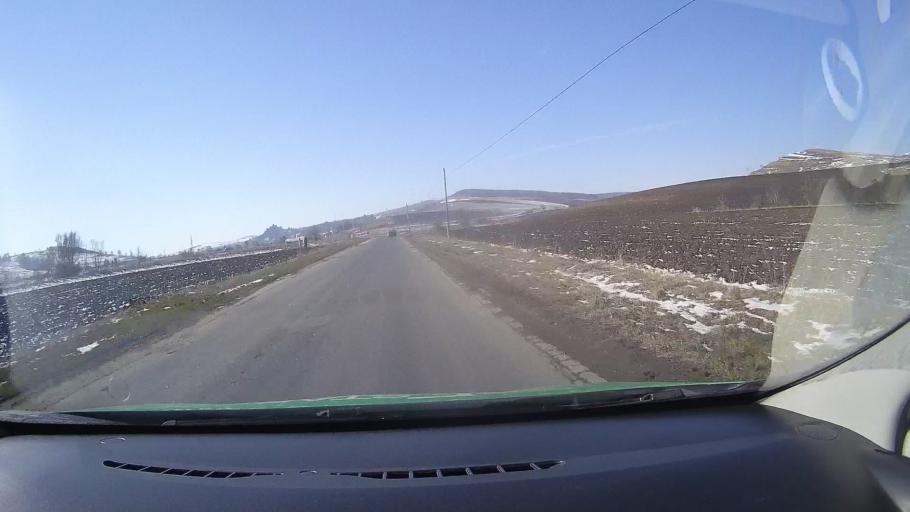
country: RO
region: Brasov
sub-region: Comuna Homorod
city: Homorod
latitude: 46.0403
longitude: 25.2523
